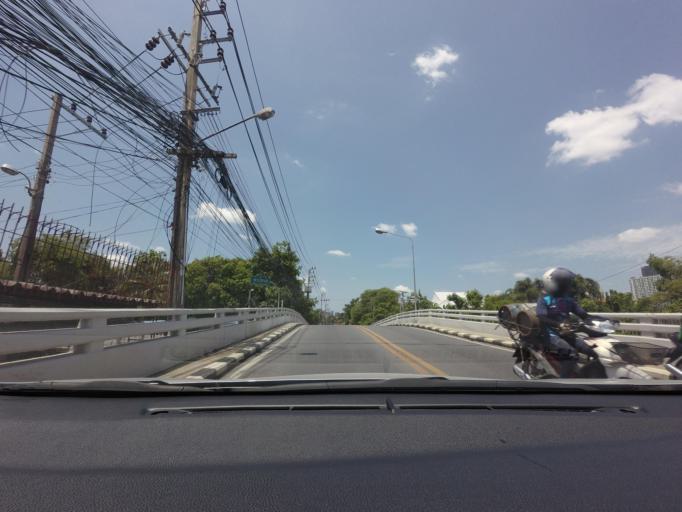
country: TH
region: Bangkok
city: Phra Khanong
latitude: 13.7157
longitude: 100.6107
